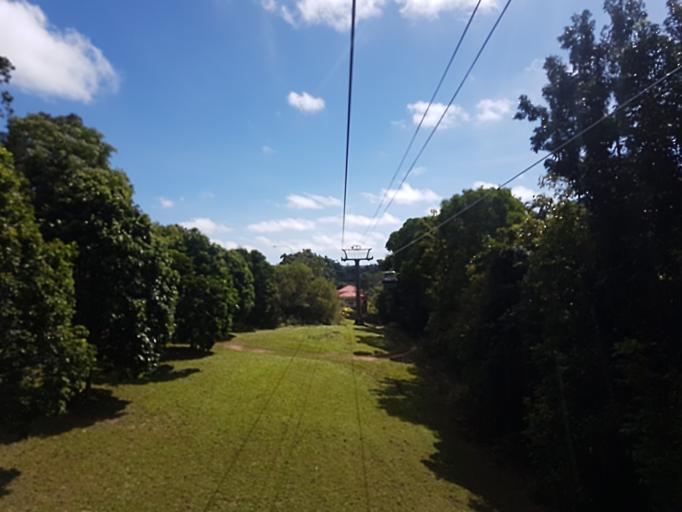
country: AU
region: Queensland
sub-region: Tablelands
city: Kuranda
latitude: -16.8208
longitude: 145.6398
